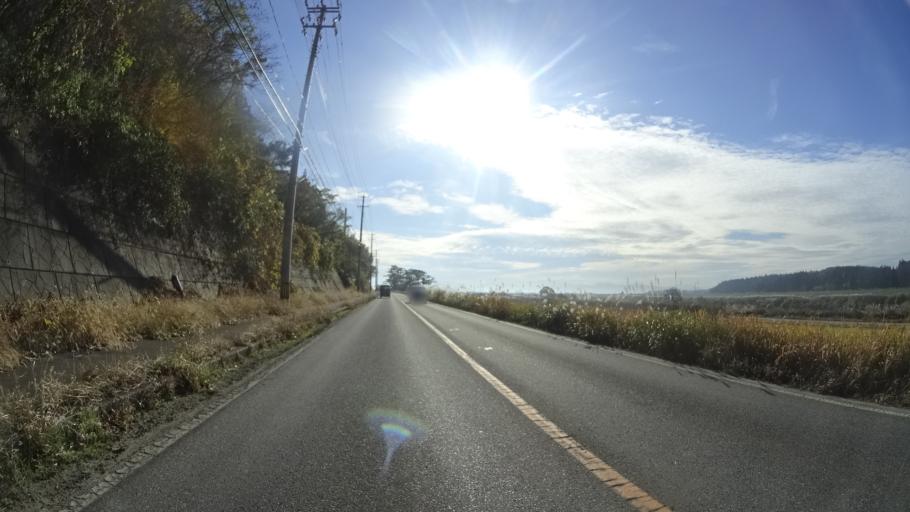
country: JP
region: Niigata
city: Yoshida-kasugacho
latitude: 37.6521
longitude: 138.8105
